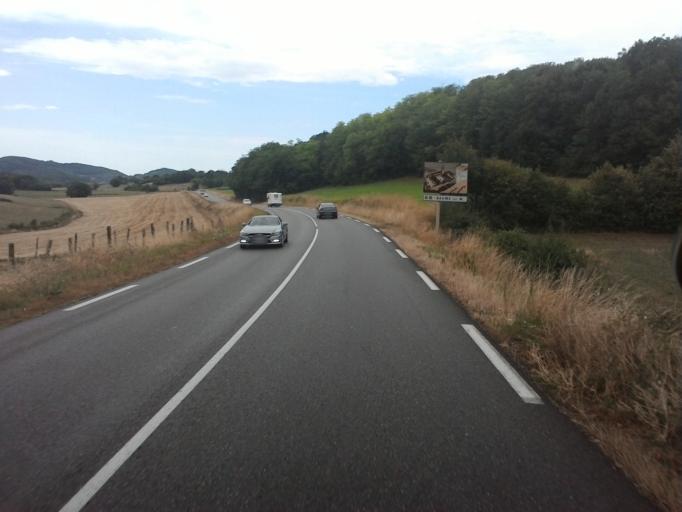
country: FR
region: Franche-Comte
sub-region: Departement du Jura
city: Poligny
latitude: 46.8295
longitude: 5.6005
